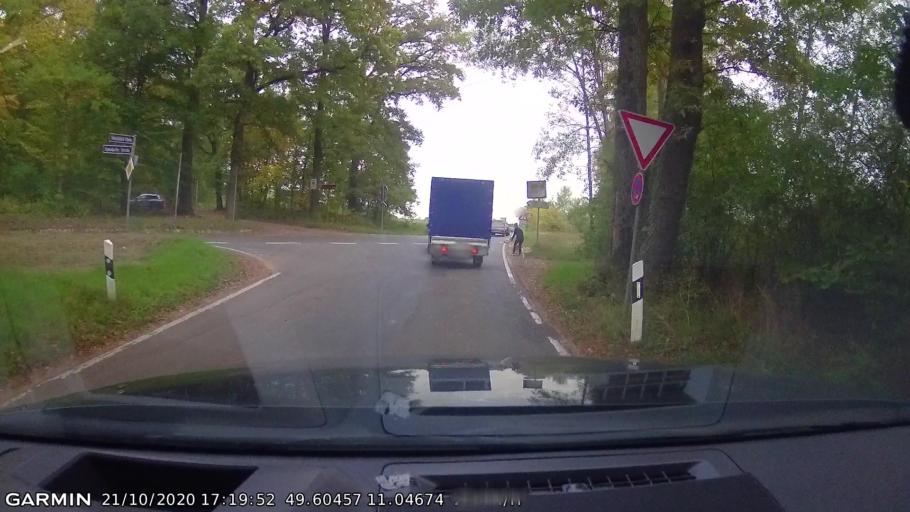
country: DE
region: Bavaria
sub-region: Regierungsbezirk Mittelfranken
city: Spardorf
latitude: 49.6046
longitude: 11.0467
